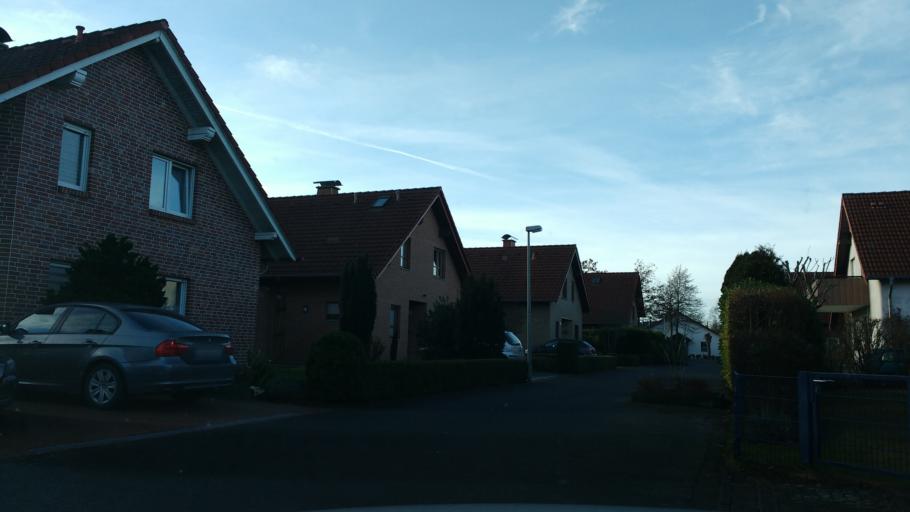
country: DE
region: North Rhine-Westphalia
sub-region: Regierungsbezirk Detmold
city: Paderborn
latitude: 51.6879
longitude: 8.6887
